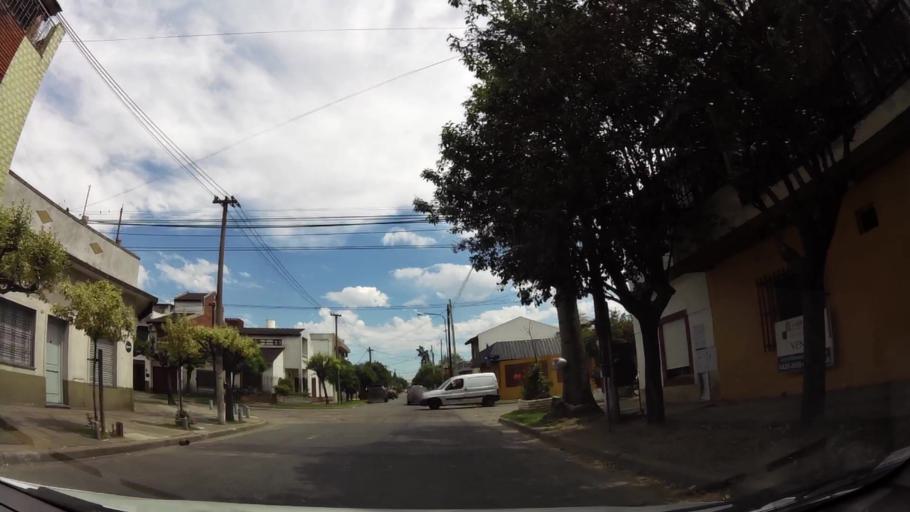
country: AR
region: Buenos Aires
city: San Justo
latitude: -34.6840
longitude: -58.5445
